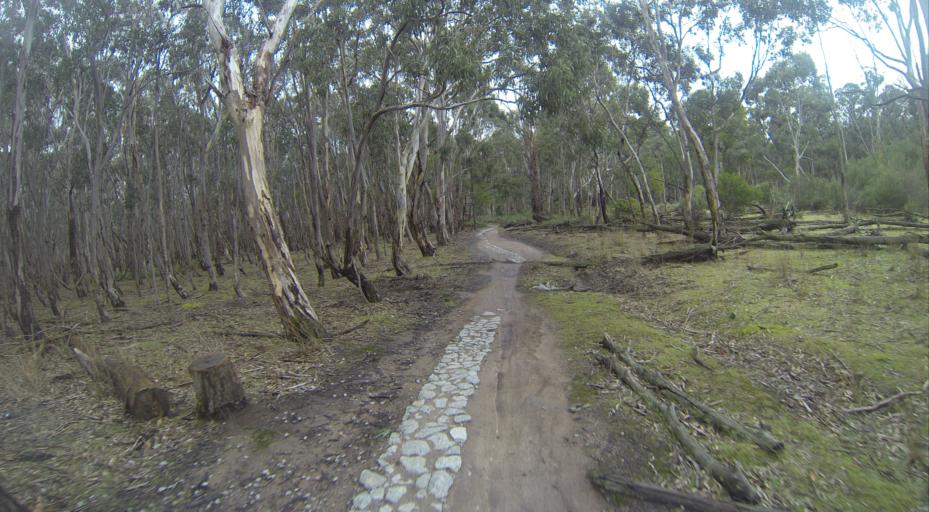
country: AU
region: Victoria
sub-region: Yarra Ranges
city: Lysterfield
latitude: -37.9474
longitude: 145.3014
